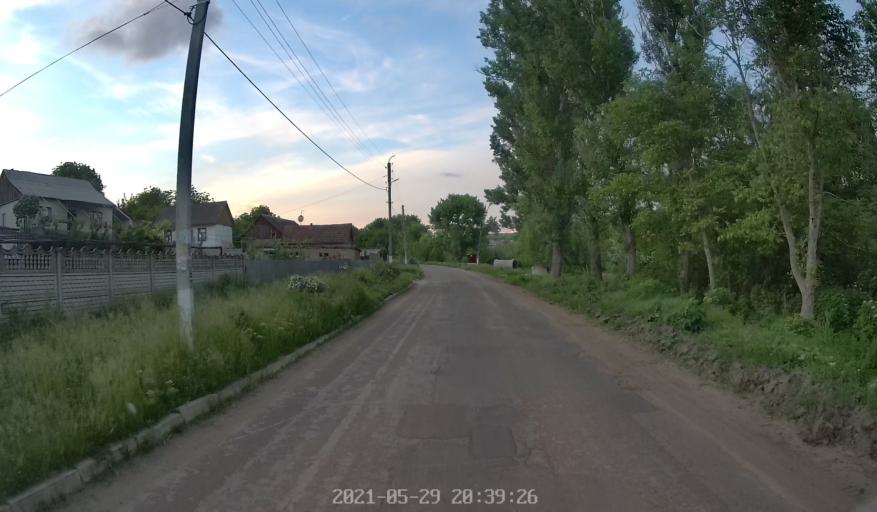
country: MD
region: Chisinau
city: Singera
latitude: 46.8357
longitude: 28.9787
